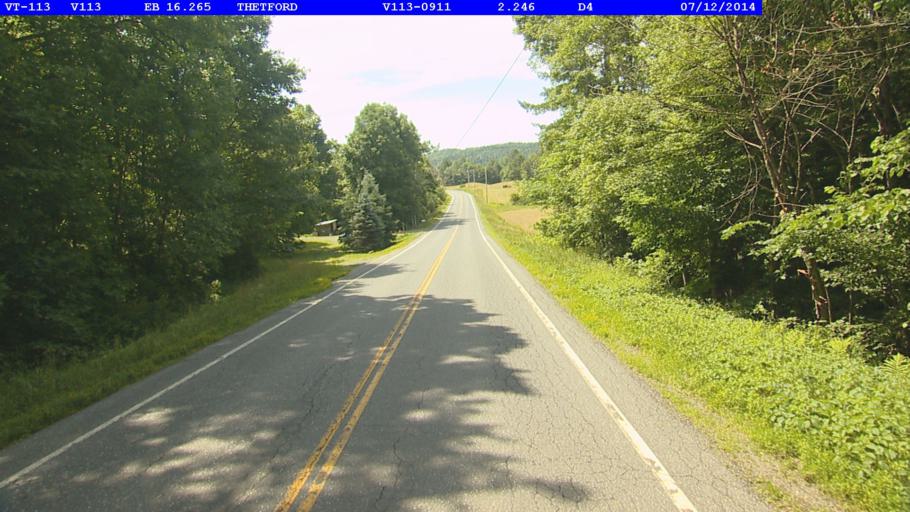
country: US
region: New Hampshire
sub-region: Grafton County
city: Lyme
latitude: 43.8664
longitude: -72.2611
